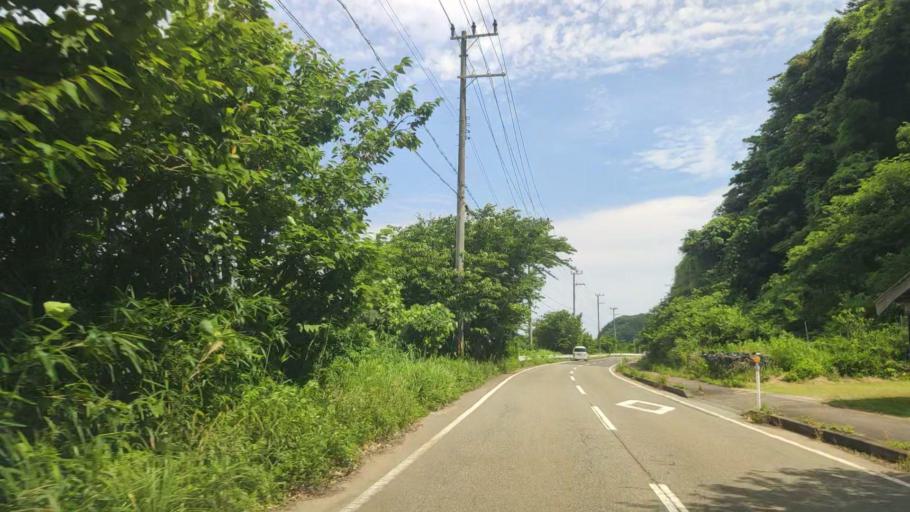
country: JP
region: Hyogo
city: Toyooka
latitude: 35.6438
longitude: 134.7622
